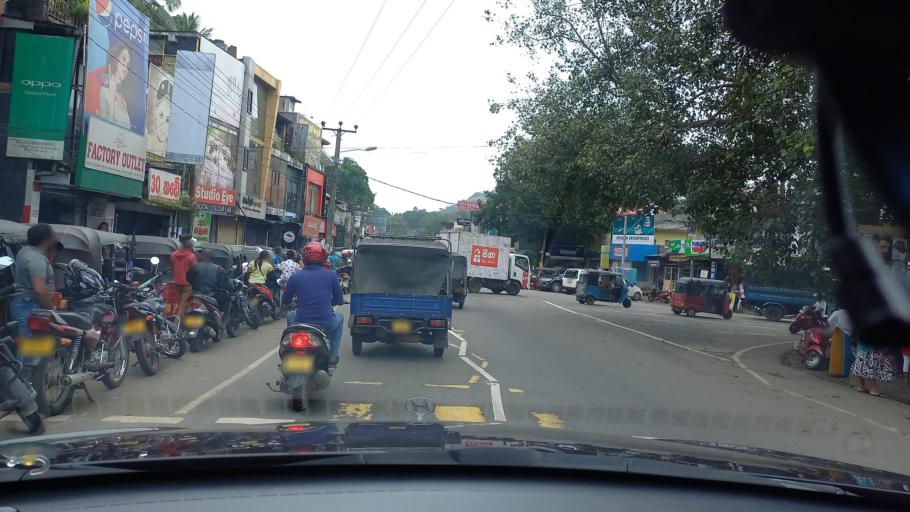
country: LK
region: Central
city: Kadugannawa
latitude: 7.2658
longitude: 80.5524
